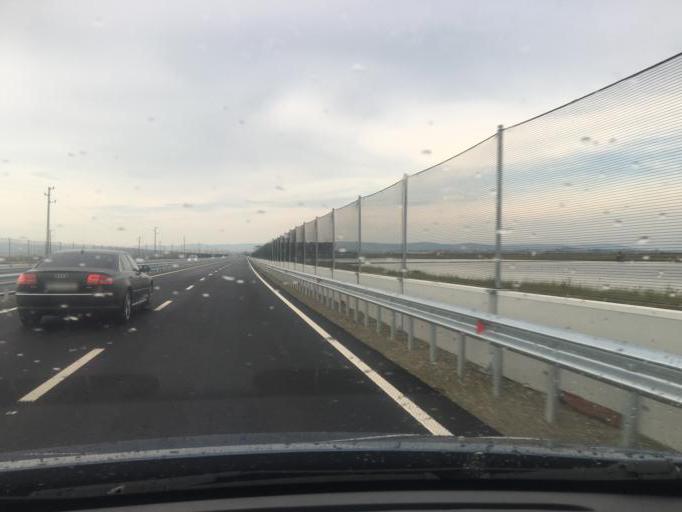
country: BG
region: Burgas
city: Aheloy
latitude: 42.6194
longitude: 27.6264
